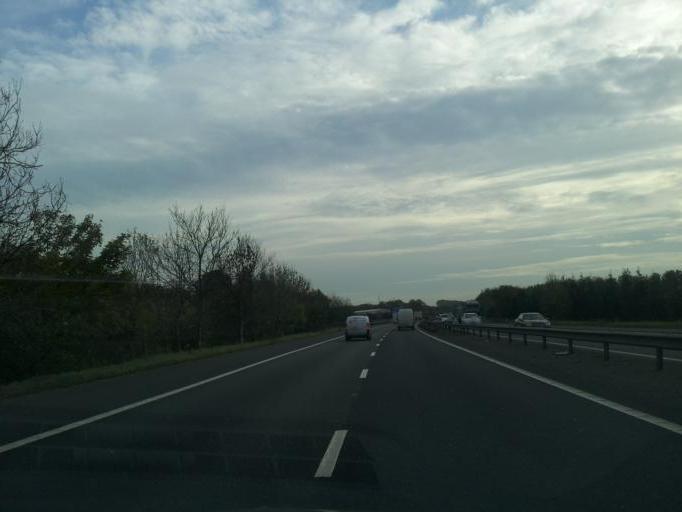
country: GB
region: England
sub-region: Cambridgeshire
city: Duxford
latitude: 52.1201
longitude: 0.1260
